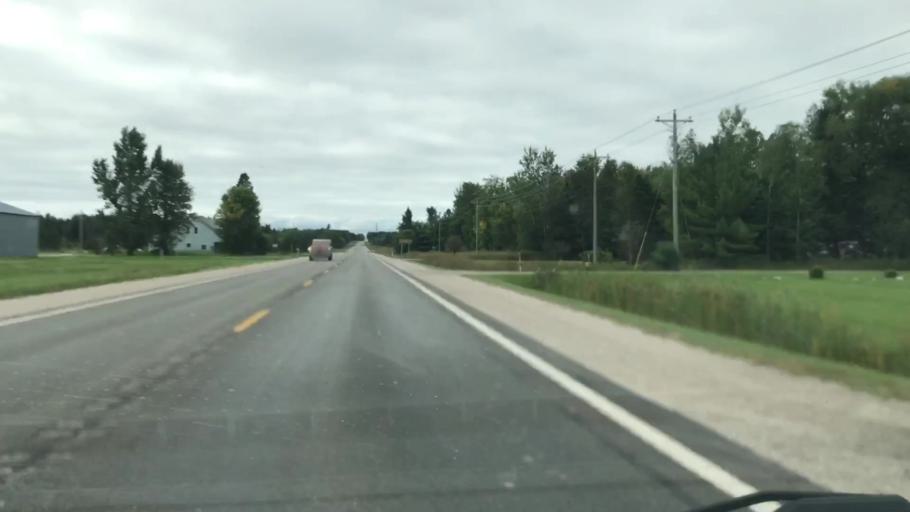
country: US
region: Michigan
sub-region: Luce County
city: Newberry
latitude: 46.1389
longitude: -85.5714
